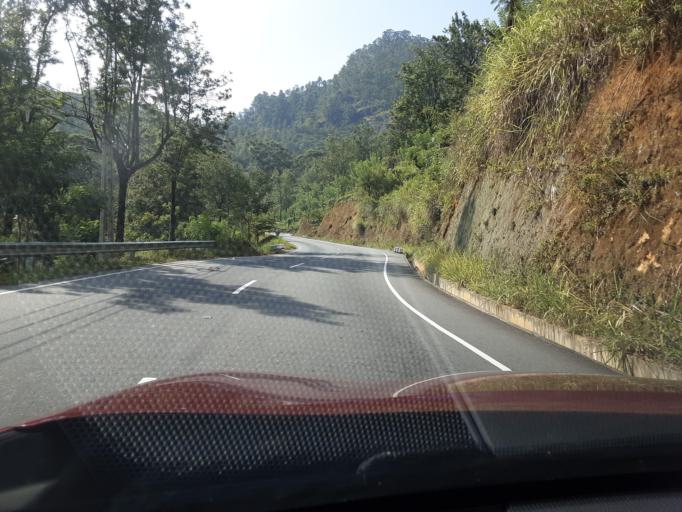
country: LK
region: Uva
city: Badulla
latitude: 6.9596
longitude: 81.1060
